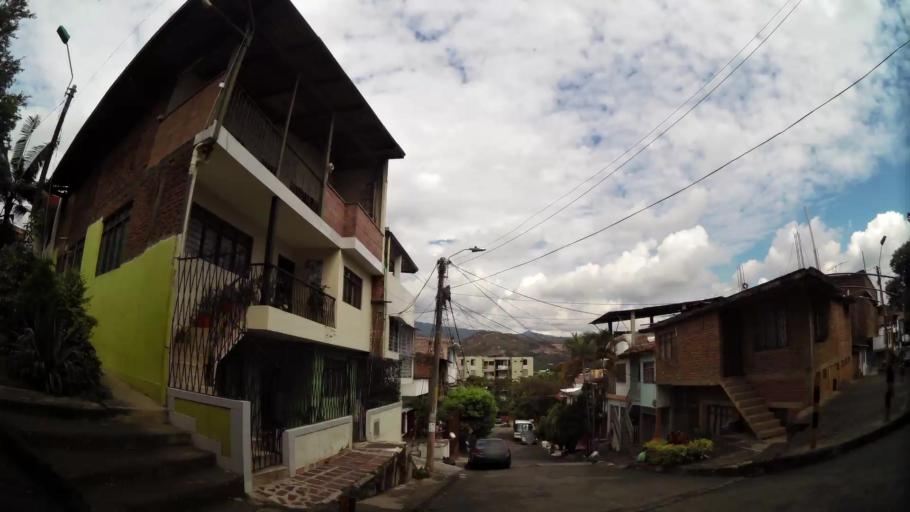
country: CO
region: Valle del Cauca
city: Cali
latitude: 3.3867
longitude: -76.5516
